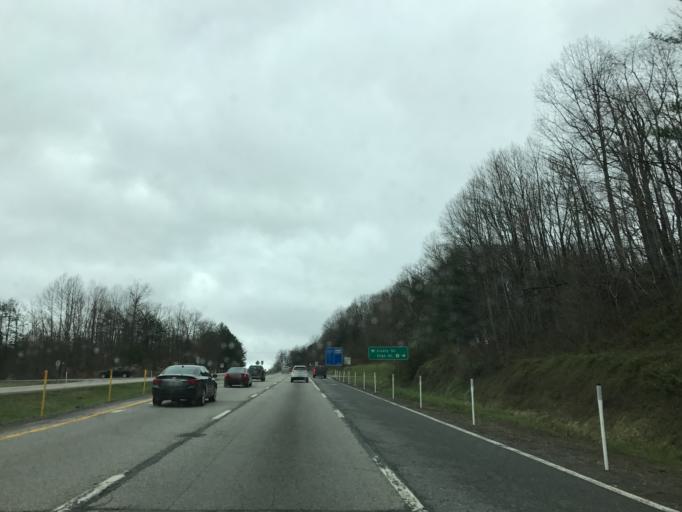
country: US
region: West Virginia
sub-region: Fayette County
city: Fayetteville
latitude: 38.0548
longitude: -81.1109
